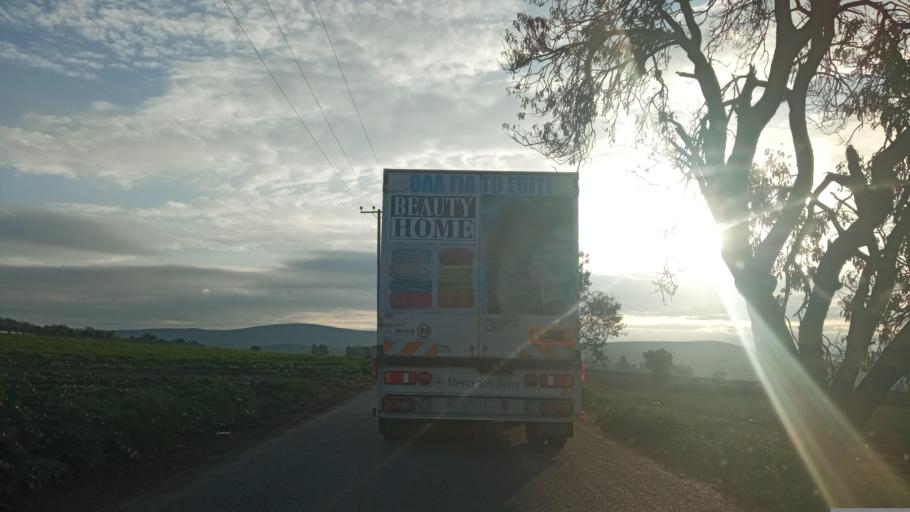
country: GR
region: Central Greece
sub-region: Nomos Evvoias
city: Psachna
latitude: 38.5758
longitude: 23.7106
